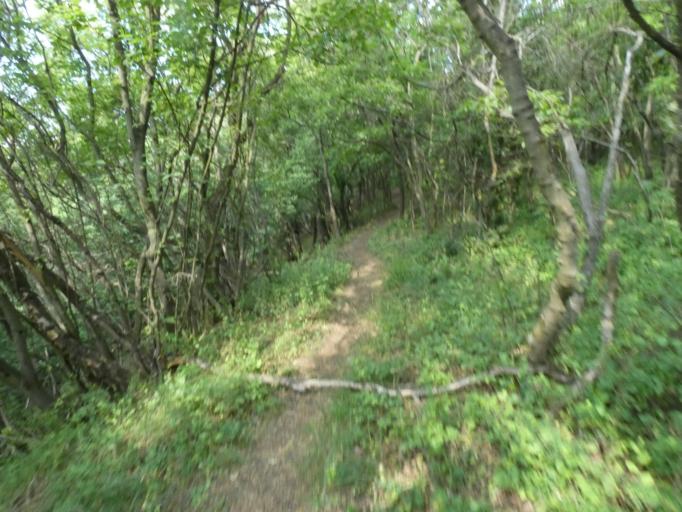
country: HU
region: Nograd
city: Szurdokpuspoki
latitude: 47.8531
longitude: 19.7086
